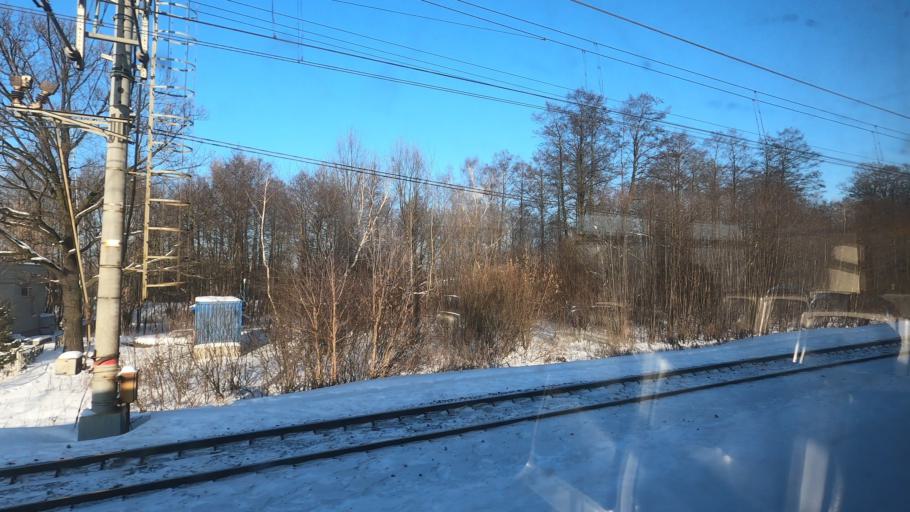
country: RU
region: Moskovskaya
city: Imeni Vorovskogo
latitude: 55.7207
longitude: 38.3503
